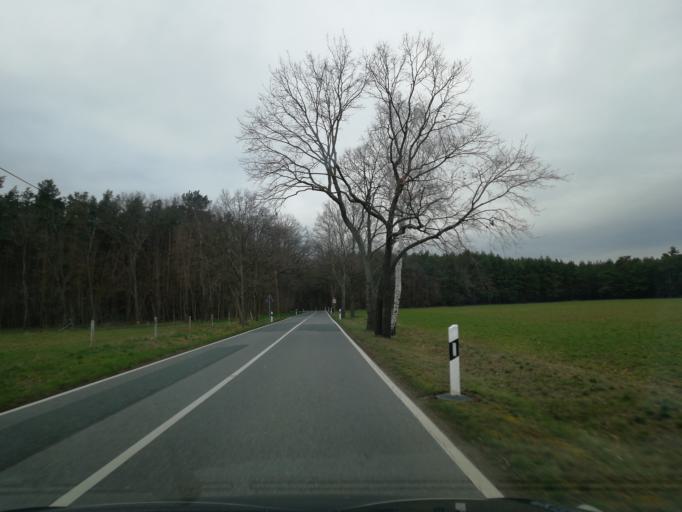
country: DE
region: Brandenburg
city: Vetschau
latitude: 51.7352
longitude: 14.0553
